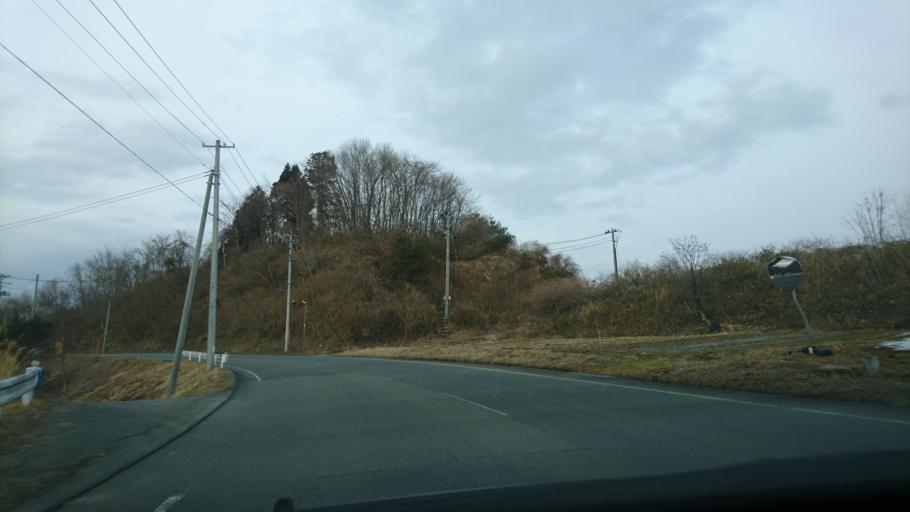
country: JP
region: Iwate
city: Ichinoseki
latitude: 38.9385
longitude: 141.3609
